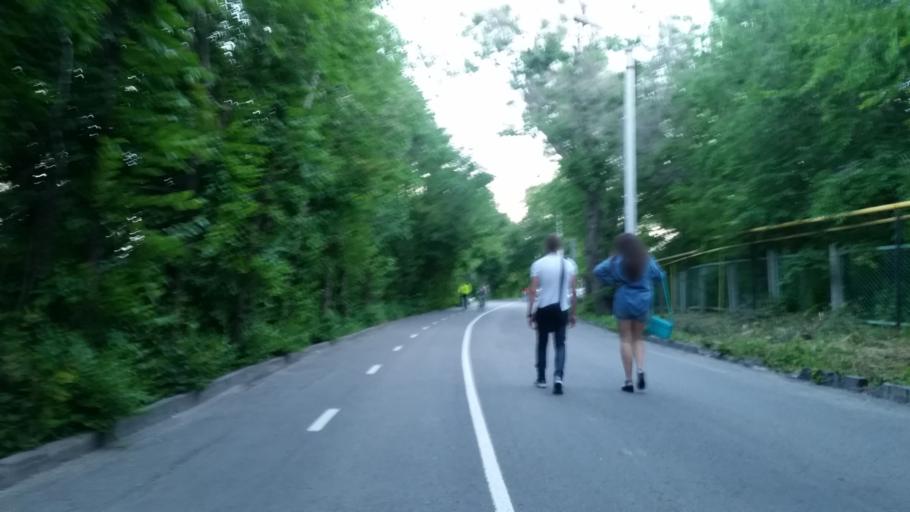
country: RU
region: Ulyanovsk
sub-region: Ulyanovskiy Rayon
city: Ulyanovsk
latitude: 54.3225
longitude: 48.4098
